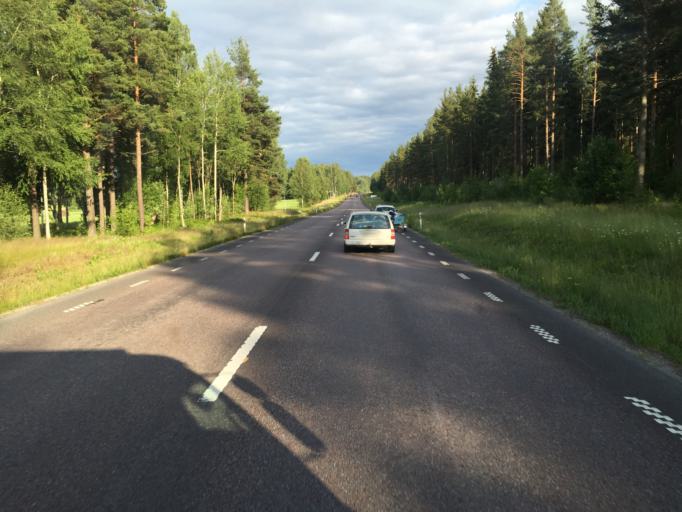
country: SE
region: Dalarna
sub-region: Borlange Kommun
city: Borlaenge
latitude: 60.5221
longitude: 15.3596
